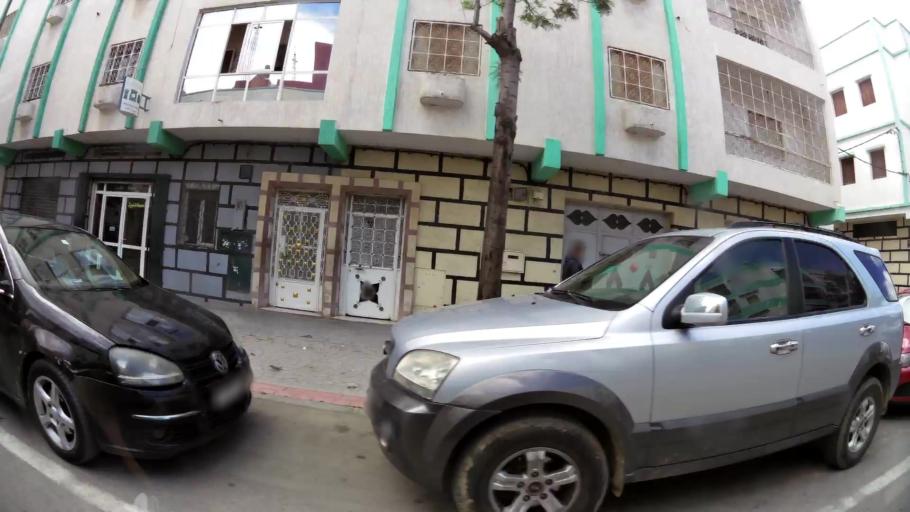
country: MA
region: Tanger-Tetouan
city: Tetouan
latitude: 35.5785
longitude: -5.3510
